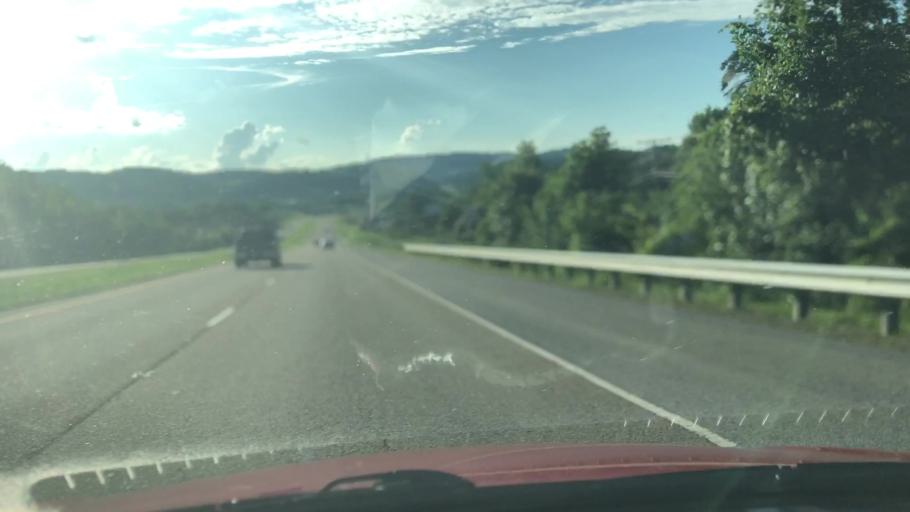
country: US
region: Tennessee
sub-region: Jefferson County
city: Dandridge
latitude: 36.0425
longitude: -83.4496
